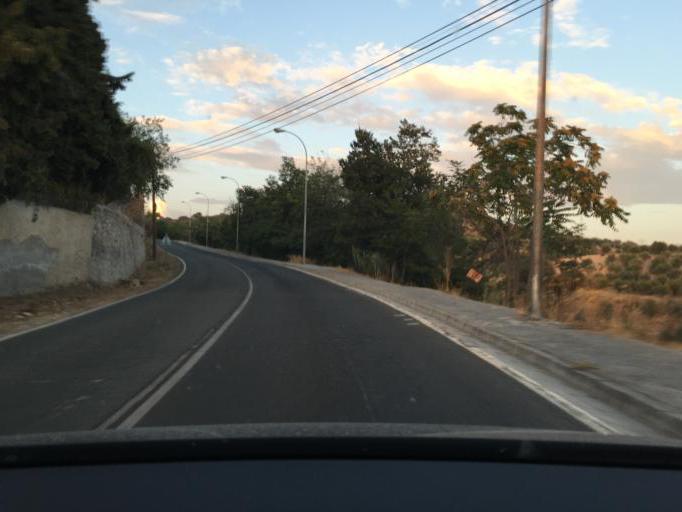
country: ES
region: Andalusia
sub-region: Provincia de Granada
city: Viznar
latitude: 37.2033
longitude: -3.5625
